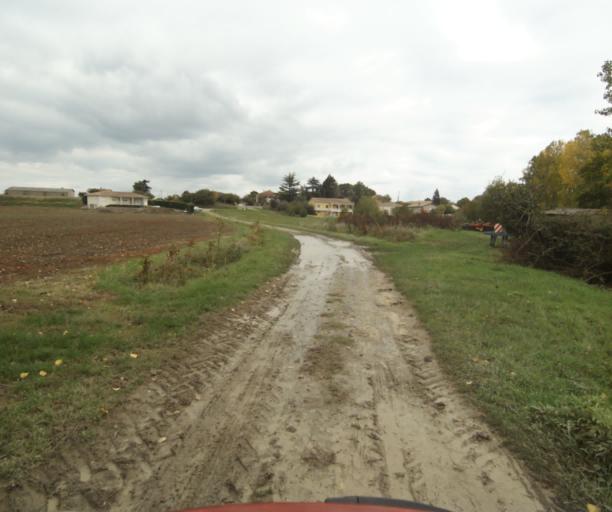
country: FR
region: Midi-Pyrenees
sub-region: Departement du Tarn-et-Garonne
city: Finhan
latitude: 43.8943
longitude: 1.2314
